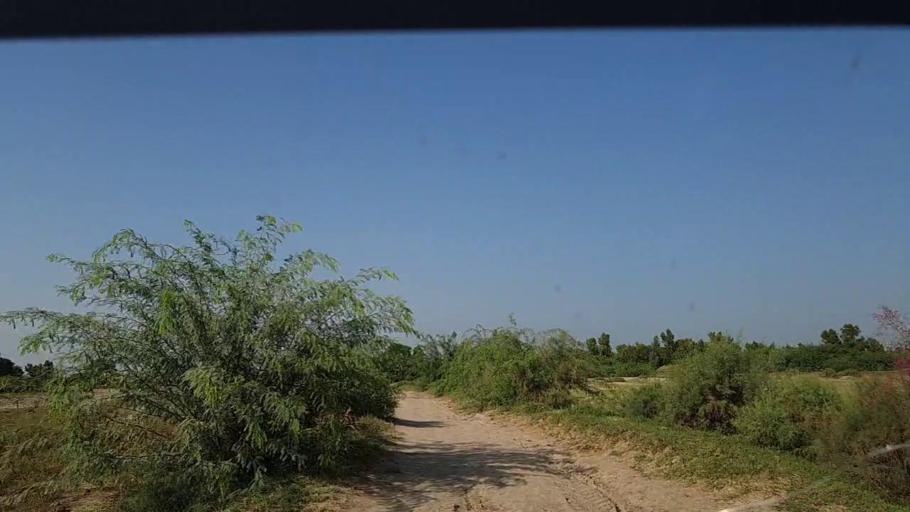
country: PK
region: Sindh
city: Adilpur
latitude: 27.9040
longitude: 69.2262
